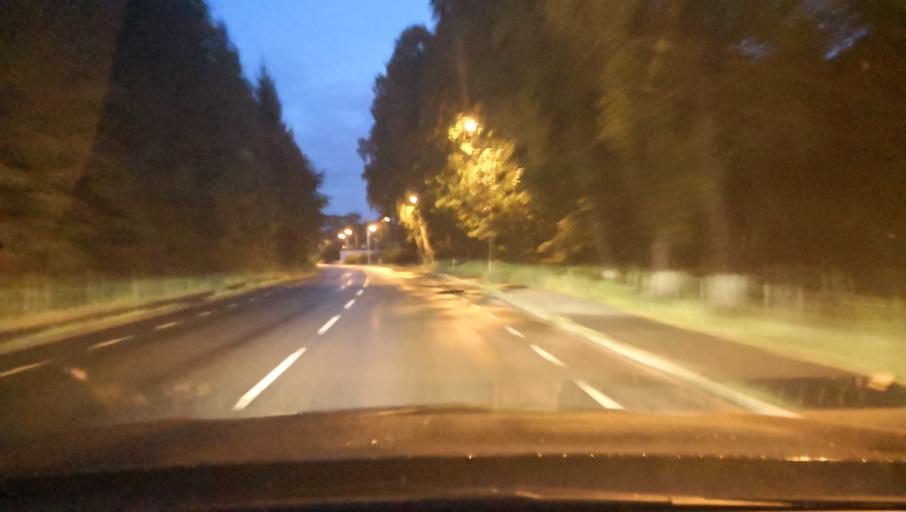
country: SE
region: Skane
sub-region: Hassleholms Kommun
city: Hastveda
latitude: 56.2923
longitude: 13.9401
